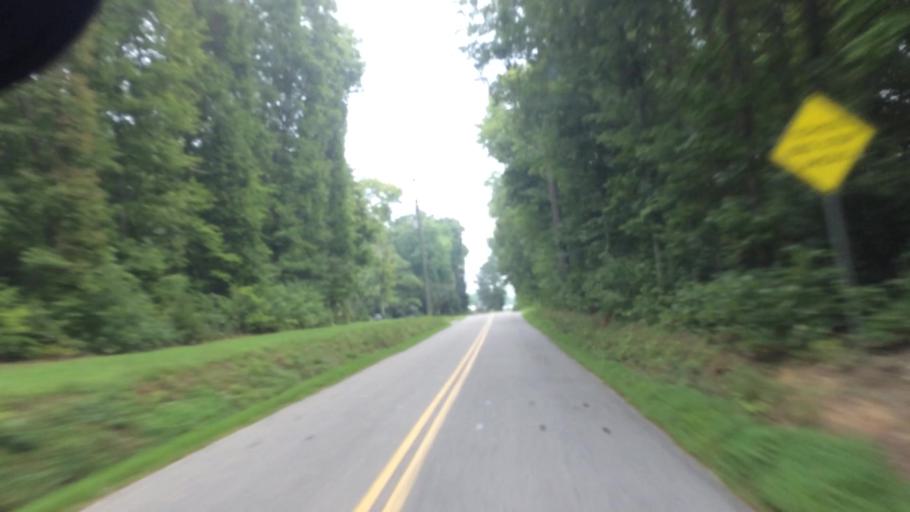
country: US
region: Virginia
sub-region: King William County
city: West Point
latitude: 37.5643
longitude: -76.7067
